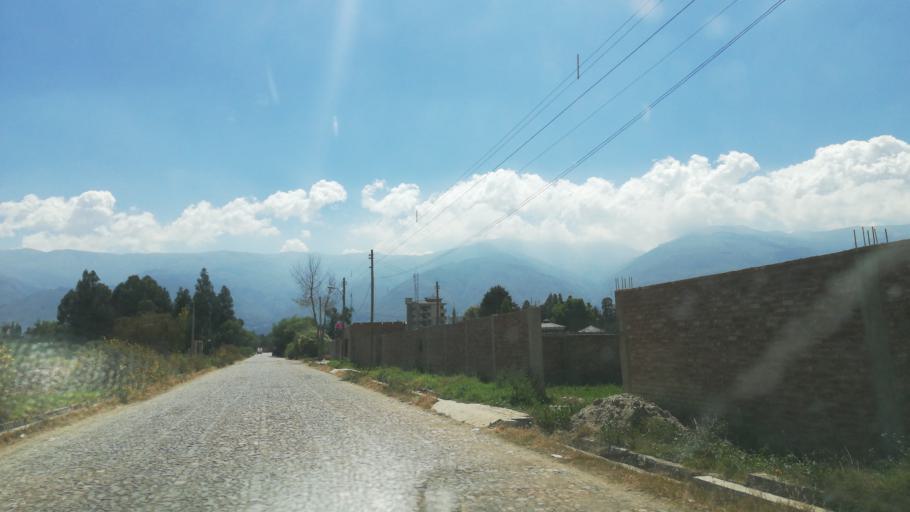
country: BO
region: Cochabamba
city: Cochabamba
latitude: -17.3718
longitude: -66.2100
